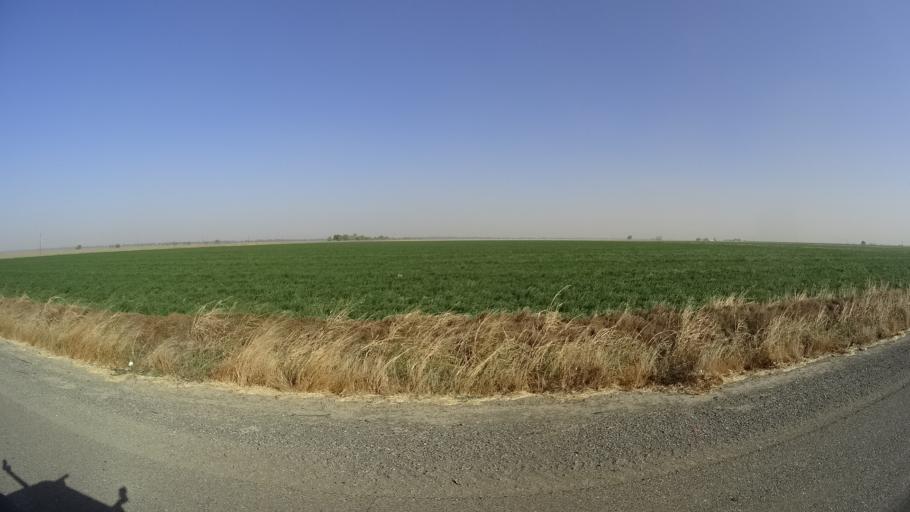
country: US
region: California
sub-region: Yolo County
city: Woodland
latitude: 38.7467
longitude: -121.7294
